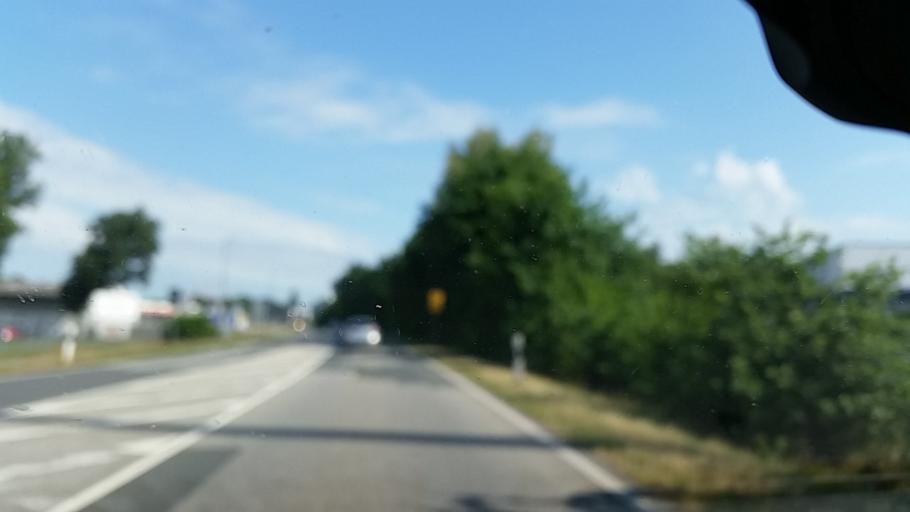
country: DE
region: Schleswig-Holstein
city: Oersdorf
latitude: 53.8281
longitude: 9.9733
